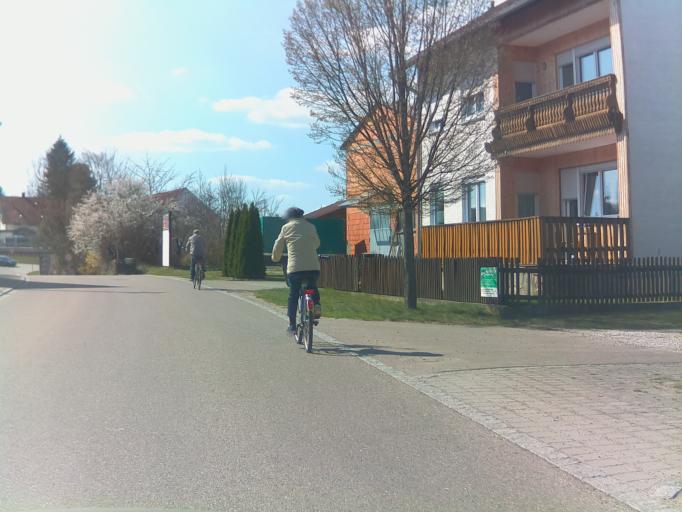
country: DE
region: Bavaria
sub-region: Swabia
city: Aichach
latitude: 48.4870
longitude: 11.1387
